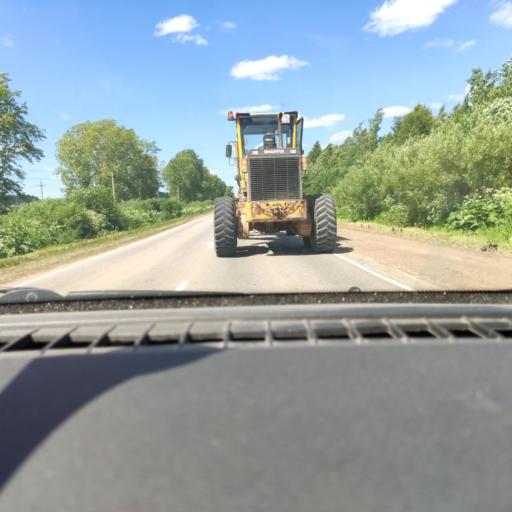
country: RU
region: Perm
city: Chaykovskaya
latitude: 58.0981
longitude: 55.5933
